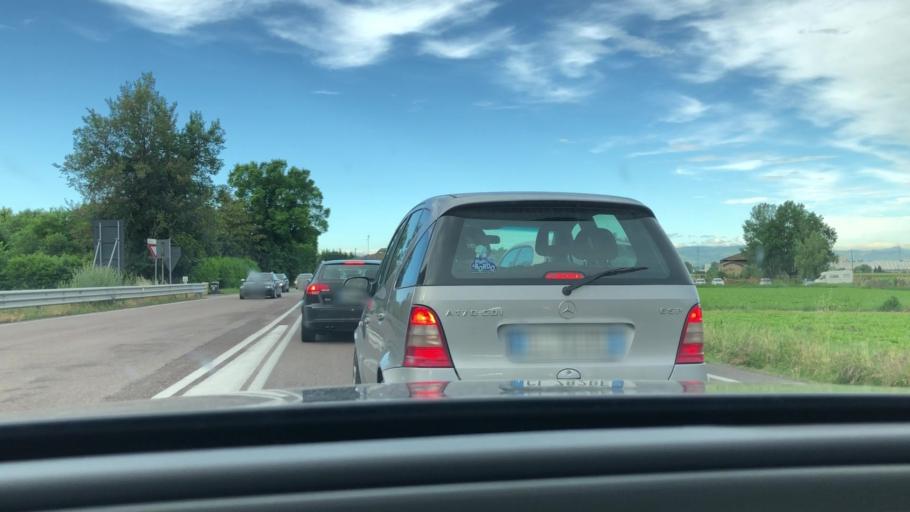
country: IT
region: Emilia-Romagna
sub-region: Provincia di Modena
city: San Damaso
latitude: 44.6099
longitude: 10.9358
